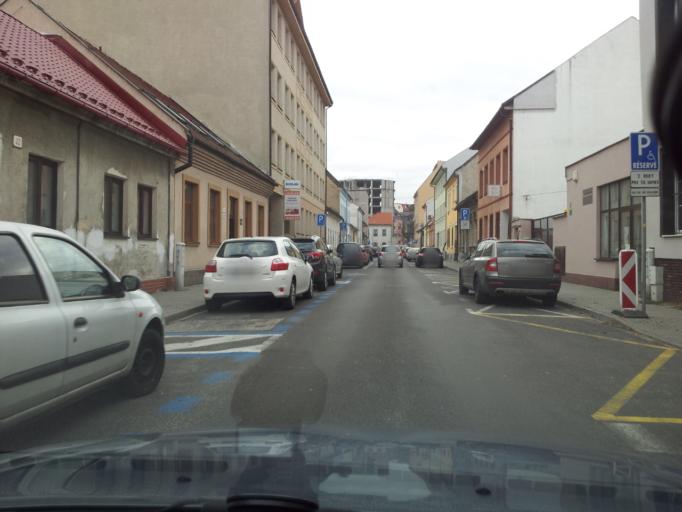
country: SK
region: Bratislavsky
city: Bratislava
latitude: 48.1588
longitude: 17.1159
